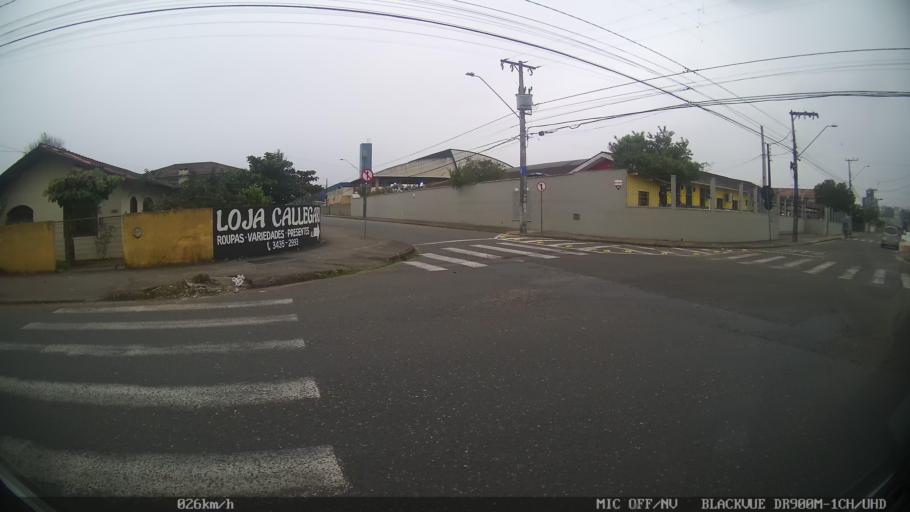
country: BR
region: Santa Catarina
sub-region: Joinville
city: Joinville
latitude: -26.2813
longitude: -48.8001
